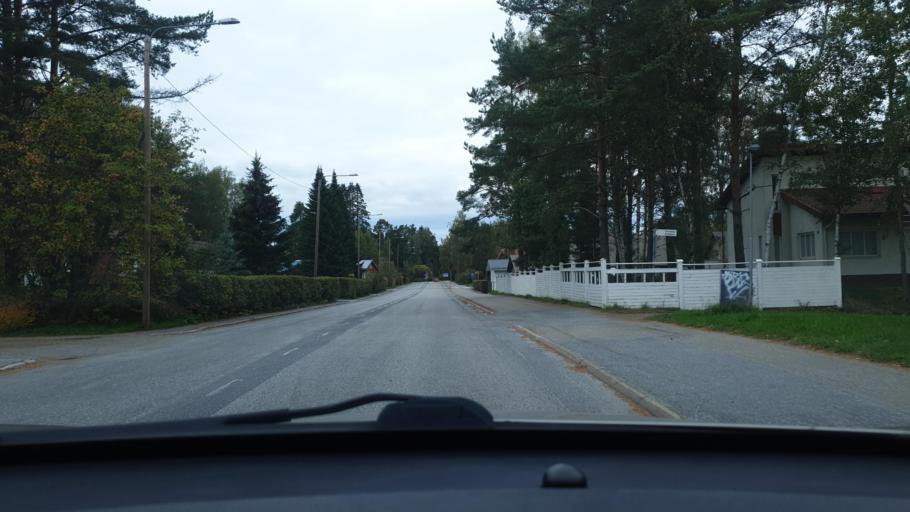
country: FI
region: Ostrobothnia
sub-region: Vaasa
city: Korsholm
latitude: 63.0971
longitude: 21.6691
